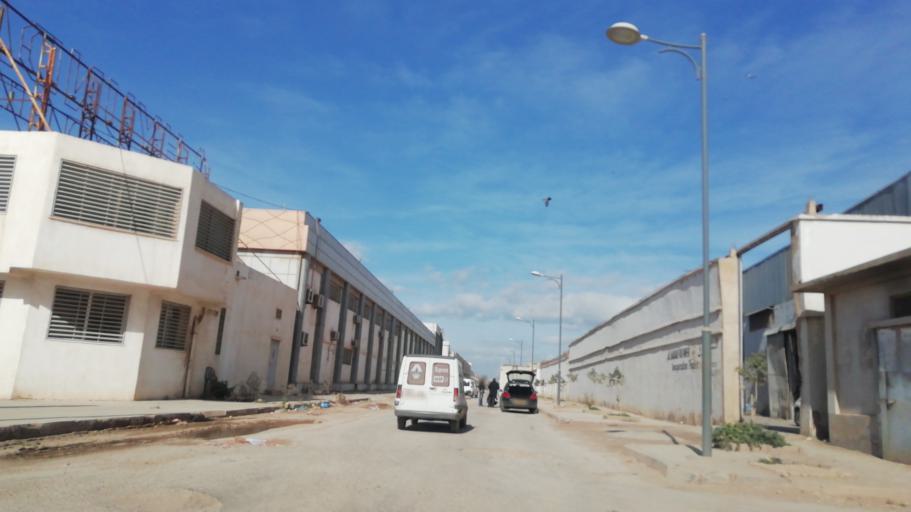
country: DZ
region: Oran
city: Es Senia
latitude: 35.6449
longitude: -0.5889
